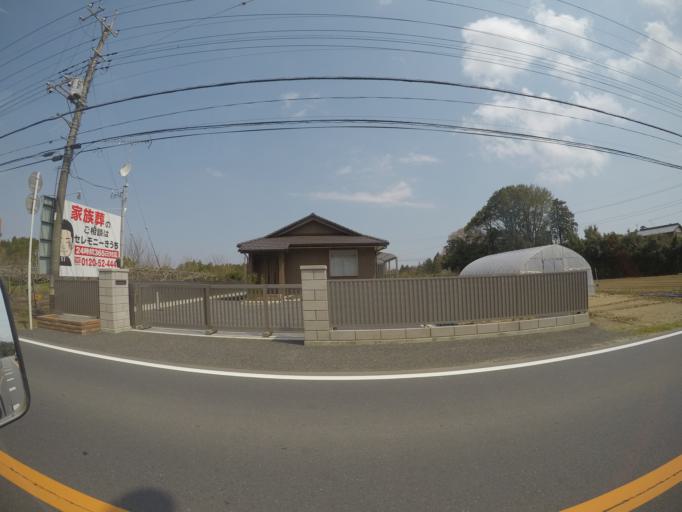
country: JP
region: Chiba
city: Sawara
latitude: 35.8650
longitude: 140.5449
